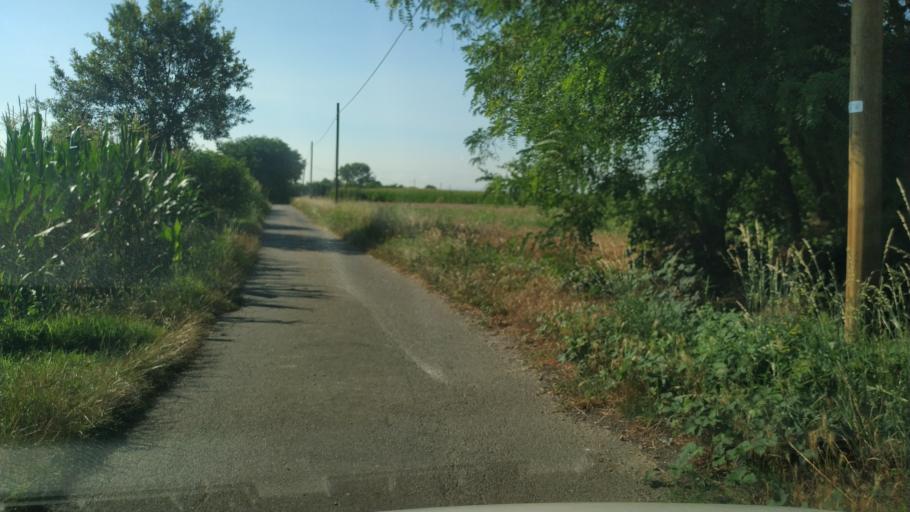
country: IT
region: Piedmont
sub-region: Provincia di Vercelli
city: Alice Castello
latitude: 45.3532
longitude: 8.0814
